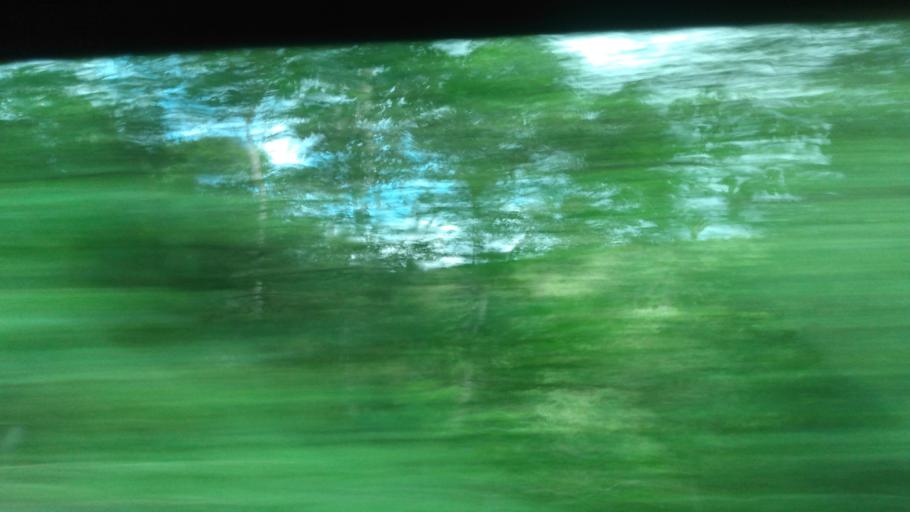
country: BR
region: Pernambuco
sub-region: Quipapa
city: Quipapa
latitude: -8.7908
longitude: -35.9833
